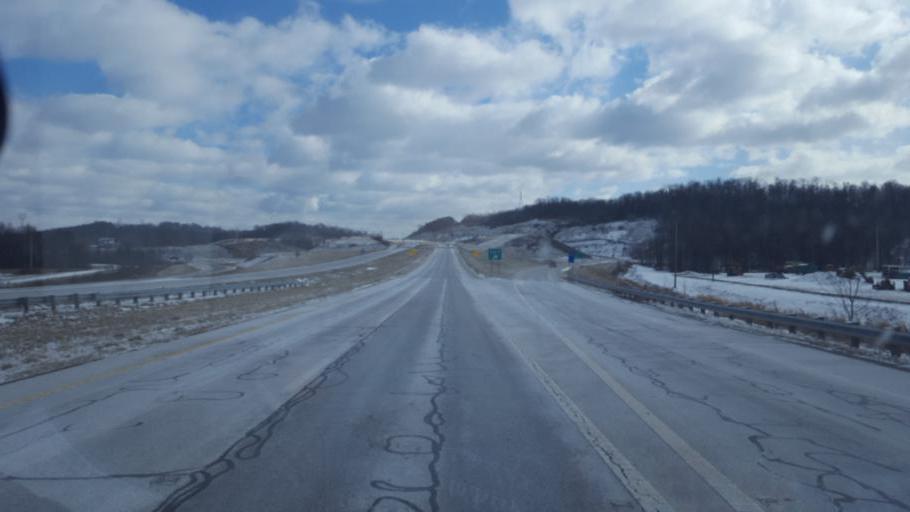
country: US
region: Ohio
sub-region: Muskingum County
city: Dresden
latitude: 40.1555
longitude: -82.0310
